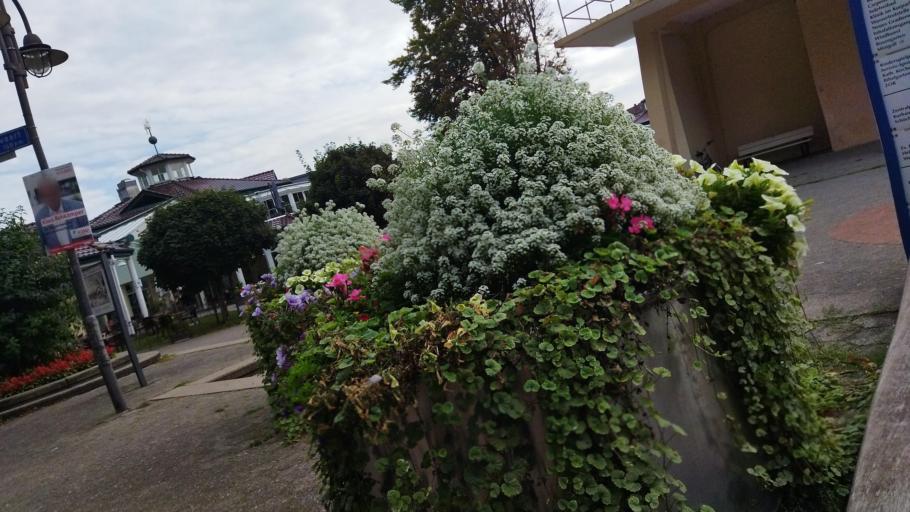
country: DE
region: Lower Saxony
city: Bad Rothenfelde
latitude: 52.1098
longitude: 8.1606
